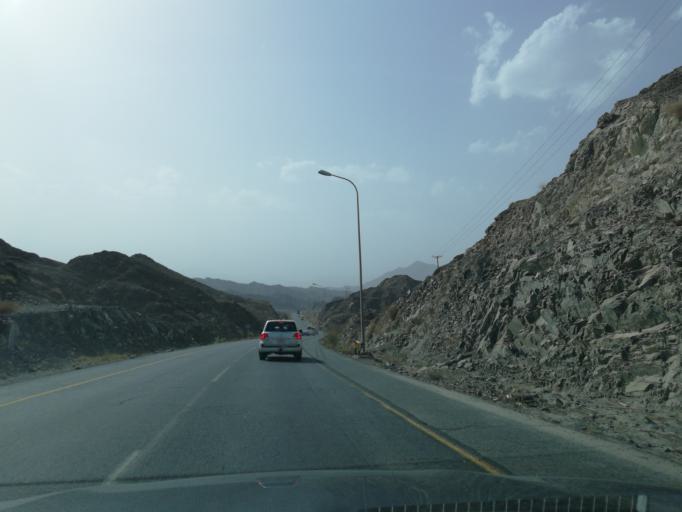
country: OM
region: Muhafazat ad Dakhiliyah
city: Sufalat Sama'il
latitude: 23.1887
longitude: 58.0908
